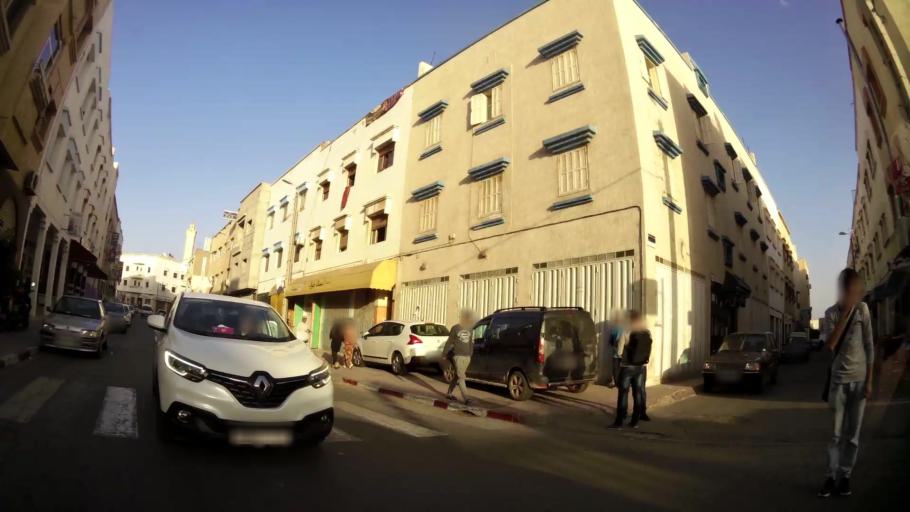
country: MA
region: Oued ed Dahab-Lagouira
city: Dakhla
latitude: 30.4115
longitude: -9.5519
